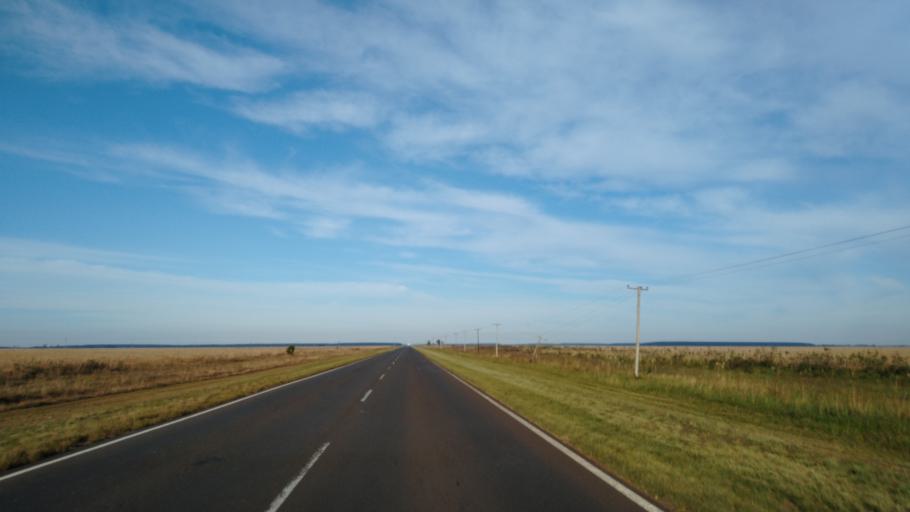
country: AR
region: Corrientes
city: La Cruz
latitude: -29.2611
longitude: -56.7486
